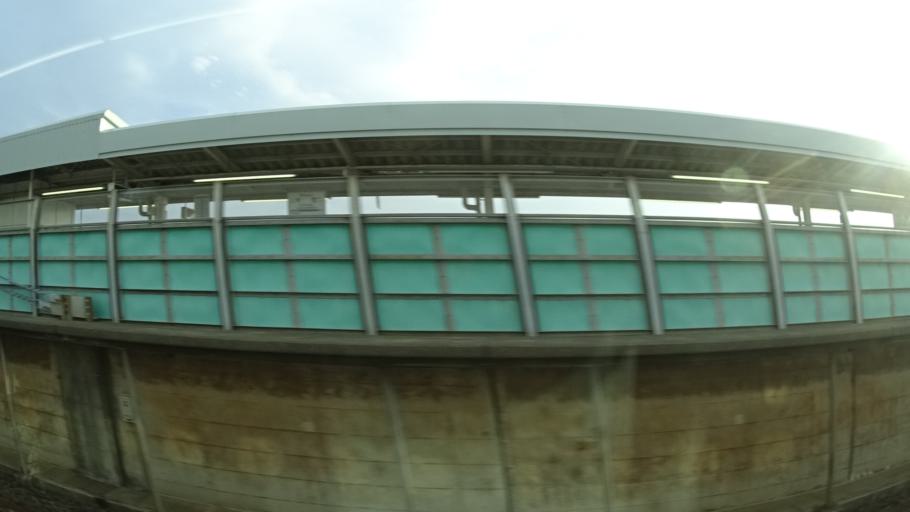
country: JP
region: Saitama
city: Okegawa
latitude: 36.0148
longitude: 139.5993
